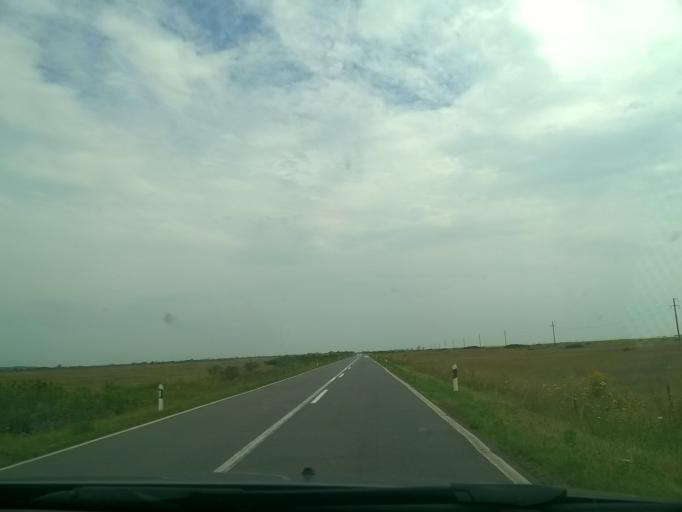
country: RS
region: Autonomna Pokrajina Vojvodina
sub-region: Srednjebanatski Okrug
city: Secanj
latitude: 45.3491
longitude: 20.7831
